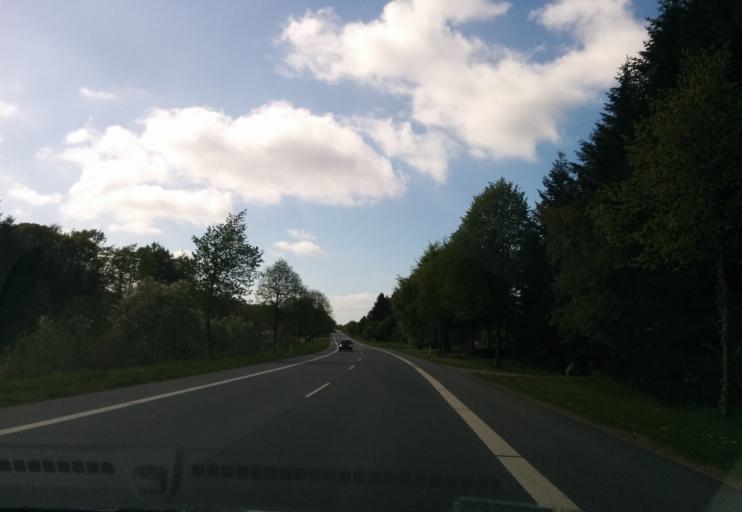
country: DK
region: South Denmark
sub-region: Assens Kommune
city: Arup
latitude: 55.4062
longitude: 10.0801
